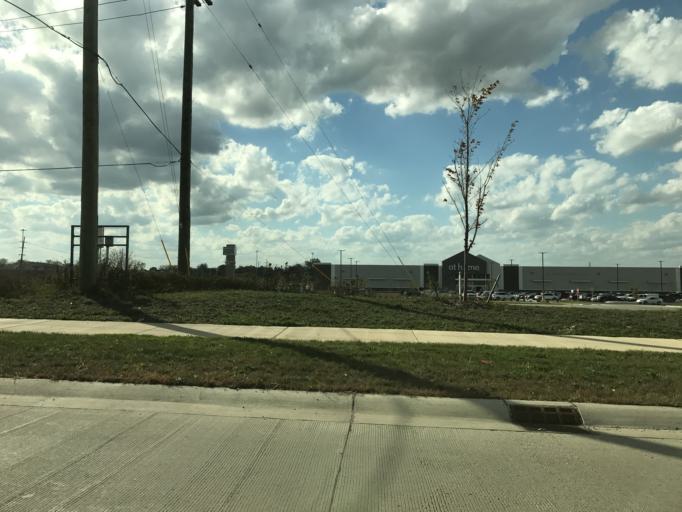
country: US
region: Michigan
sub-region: Oakland County
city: Wixom
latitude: 42.5004
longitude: -83.5363
